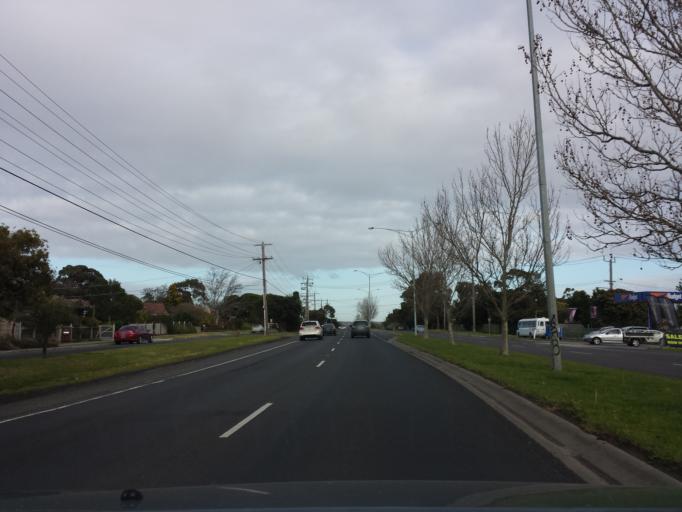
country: AU
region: Victoria
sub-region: Knox
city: Knoxfield
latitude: -37.8844
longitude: 145.2692
